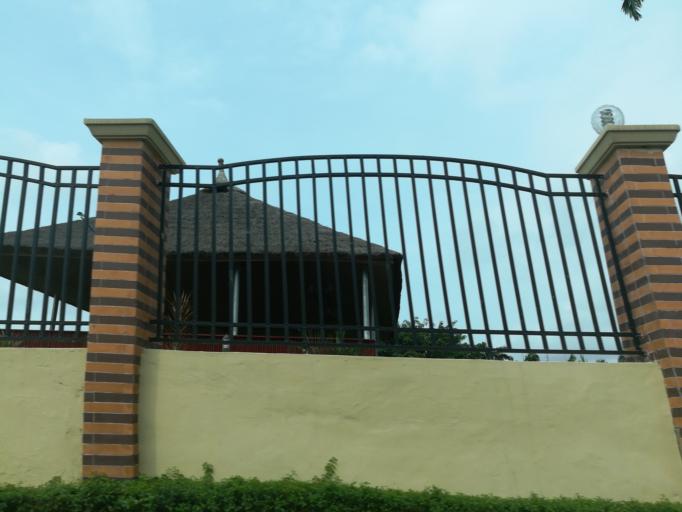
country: NG
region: Lagos
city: Ikeja
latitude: 6.6140
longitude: 3.3651
